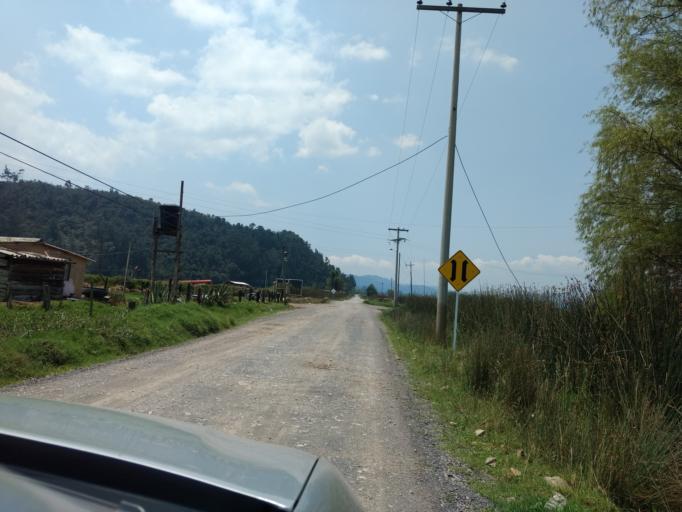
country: CO
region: Boyaca
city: Raquira
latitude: 5.4973
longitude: -73.7109
